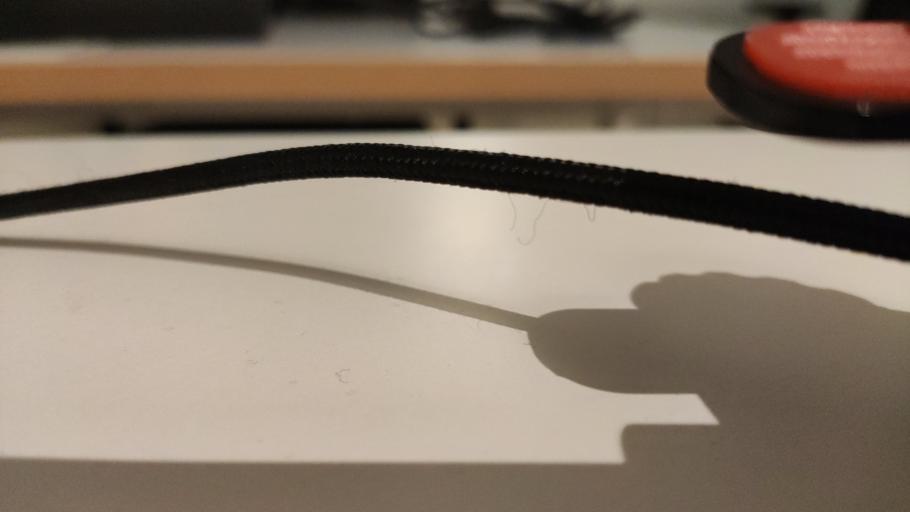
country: RU
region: Moskovskaya
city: Novosin'kovo
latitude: 56.3931
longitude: 37.2856
